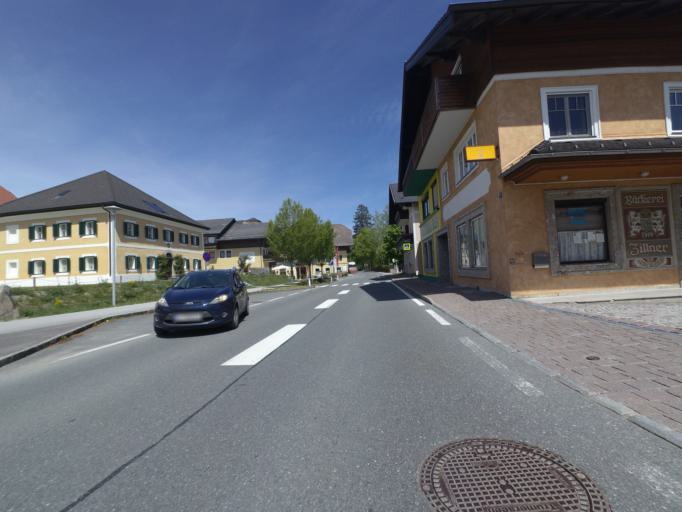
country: AT
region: Salzburg
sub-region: Politischer Bezirk Salzburg-Umgebung
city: Seeham
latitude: 47.9680
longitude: 13.0785
